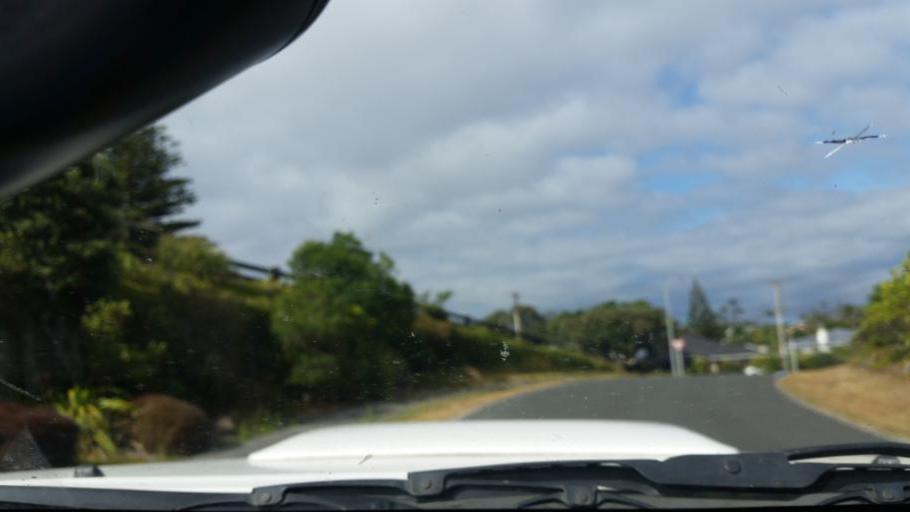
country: NZ
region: Northland
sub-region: Kaipara District
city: Dargaville
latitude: -35.9494
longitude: 173.7485
